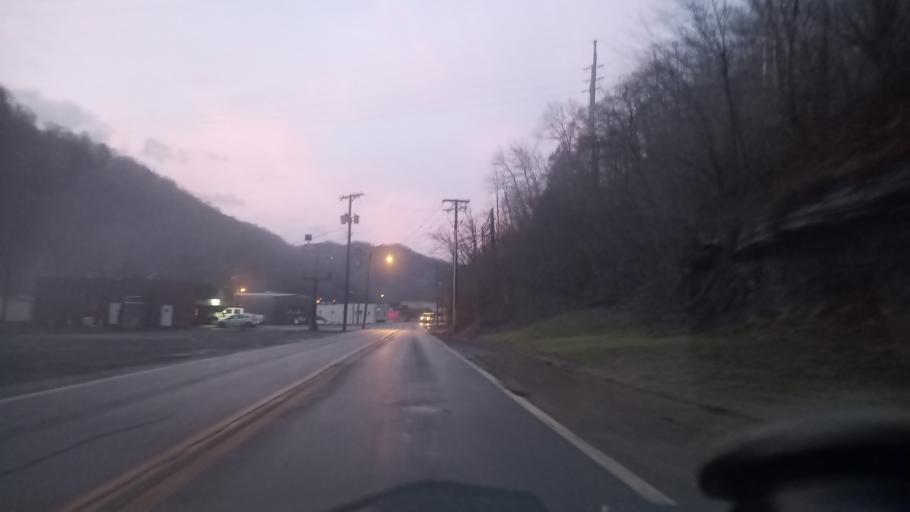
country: US
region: West Virginia
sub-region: Logan County
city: Mallory
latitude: 37.7406
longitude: -81.8762
